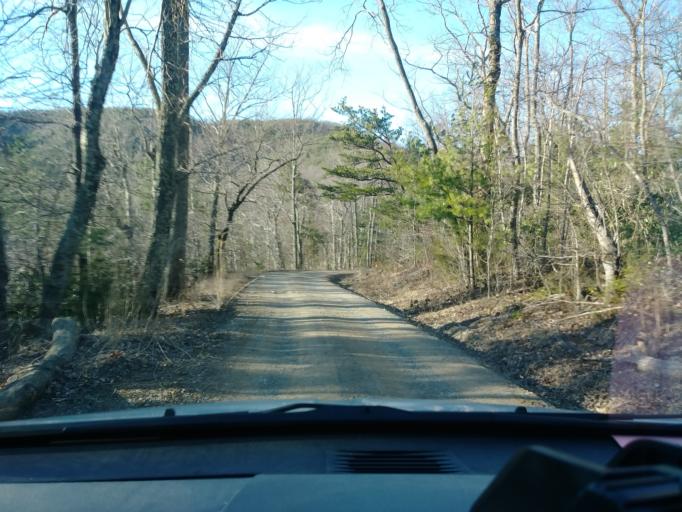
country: US
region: Tennessee
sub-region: Greene County
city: Tusculum
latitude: 36.0702
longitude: -82.6870
